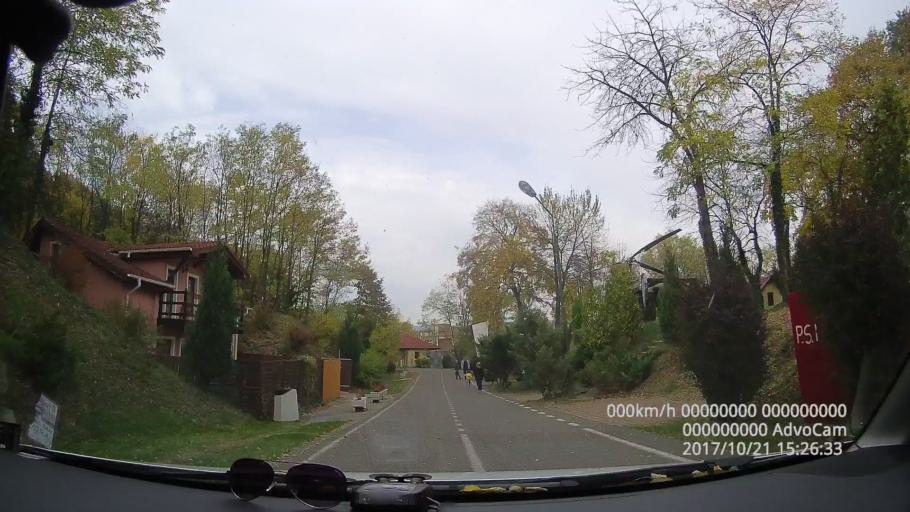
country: RO
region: Hunedoara
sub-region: Municipiul Deva
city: Deva
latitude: 45.8698
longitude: 22.9206
